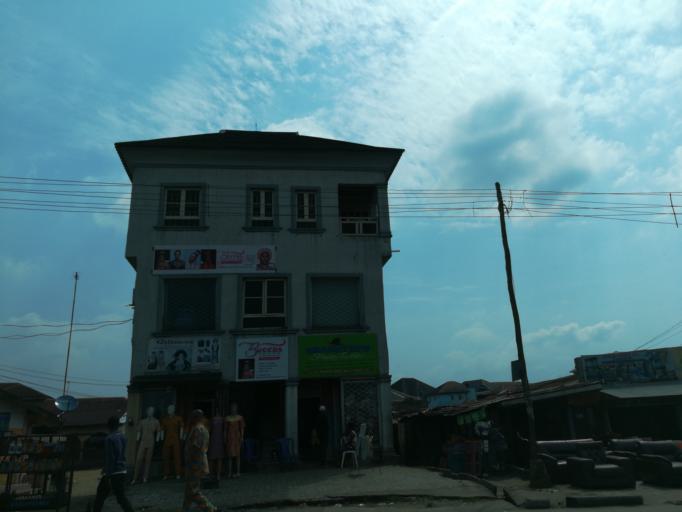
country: NG
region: Rivers
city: Port Harcourt
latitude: 4.8288
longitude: 6.9816
